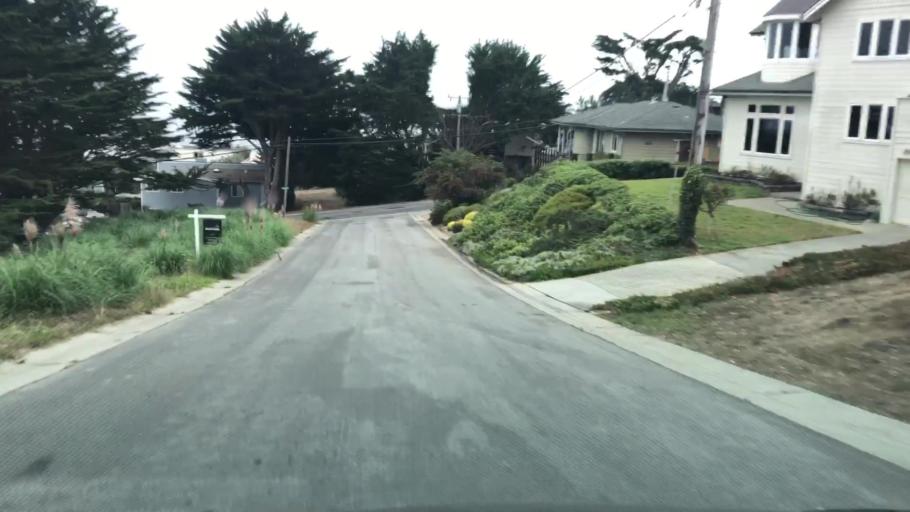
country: US
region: California
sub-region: San Mateo County
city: Montara
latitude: 37.5374
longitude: -122.5158
